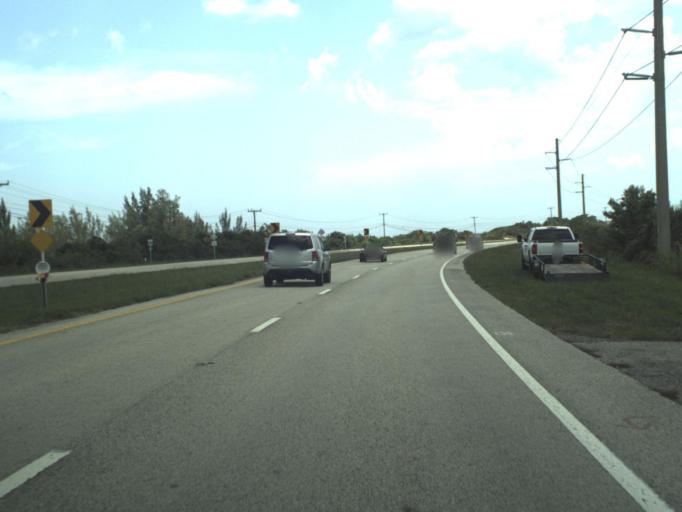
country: US
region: Florida
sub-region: Martin County
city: Hobe Sound
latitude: 27.0427
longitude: -80.1155
